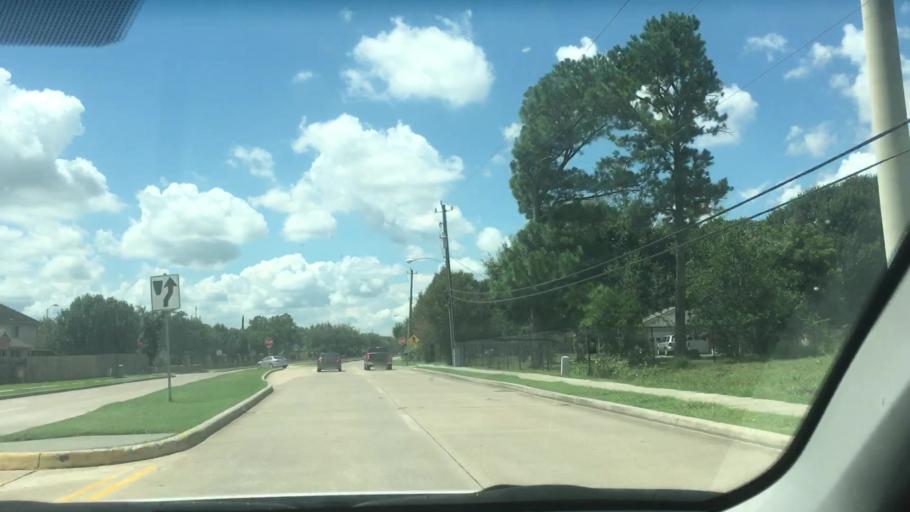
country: US
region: Texas
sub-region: Fort Bend County
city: Fifth Street
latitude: 29.6084
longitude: -95.5449
